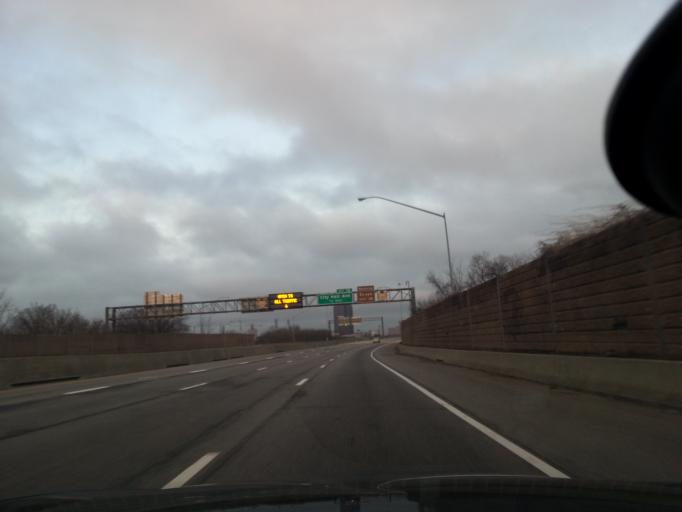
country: US
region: Virginia
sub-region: City of Norfolk
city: Norfolk
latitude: 36.8448
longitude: -76.2713
